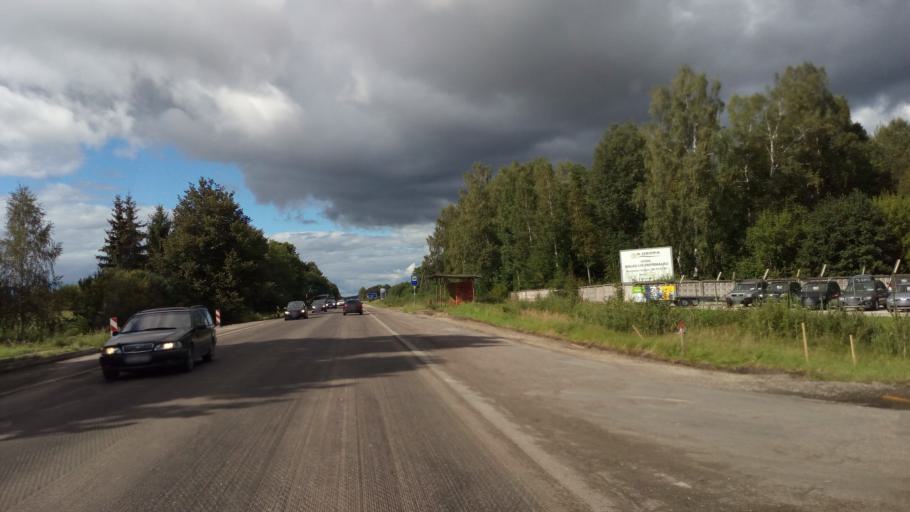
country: LV
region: Tukuma Rajons
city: Tukums
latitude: 56.9307
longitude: 23.2109
